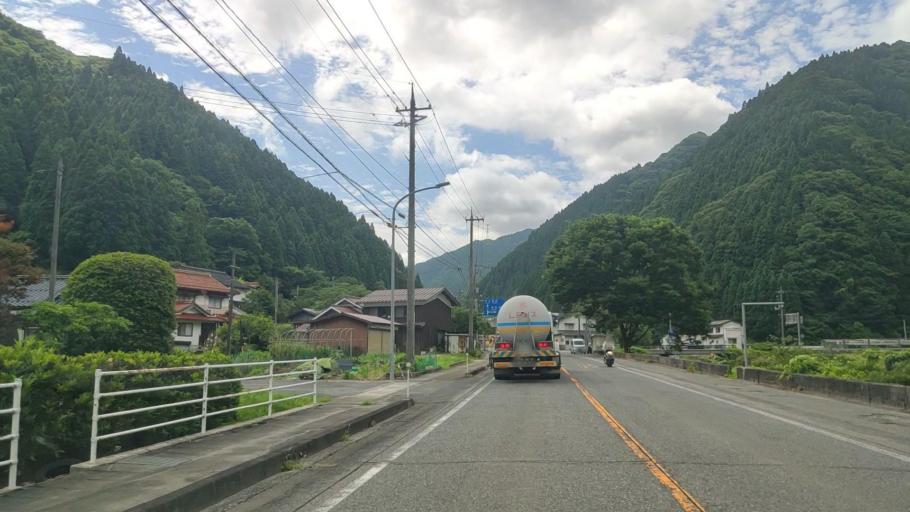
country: JP
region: Tottori
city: Yonago
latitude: 35.2286
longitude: 133.4439
